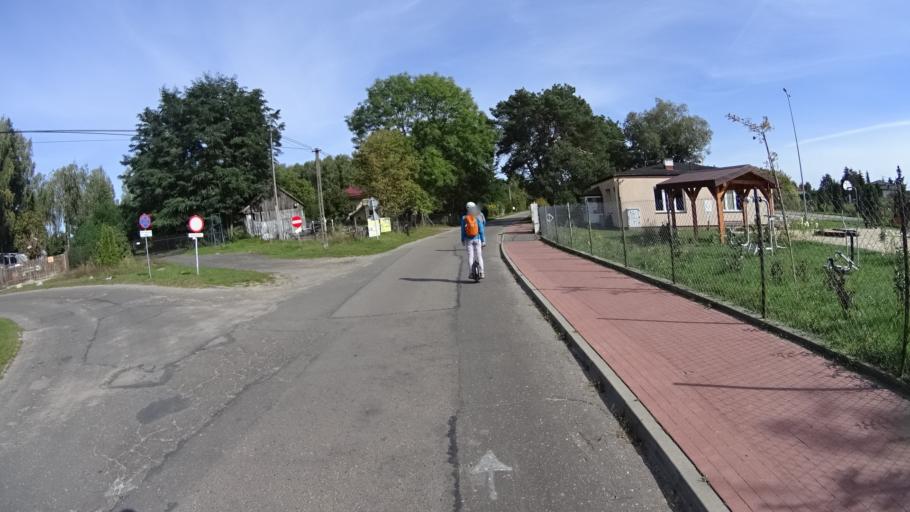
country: PL
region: Masovian Voivodeship
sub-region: Powiat legionowski
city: Serock
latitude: 52.4739
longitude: 21.0704
